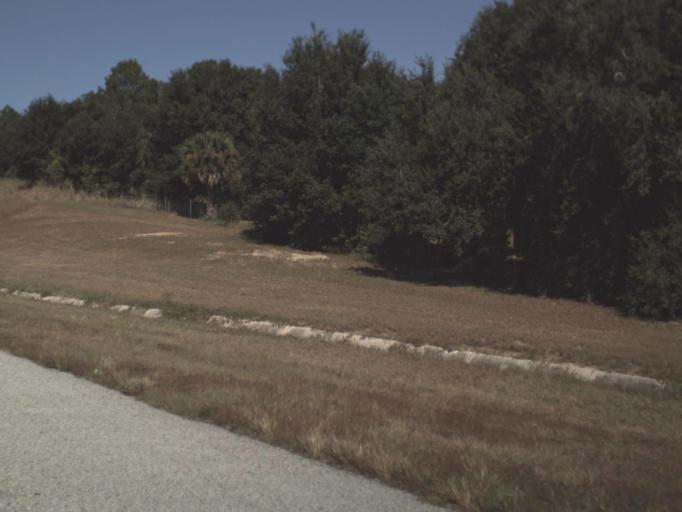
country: US
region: Florida
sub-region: Lake County
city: Montverde
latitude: 28.5696
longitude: -81.6929
